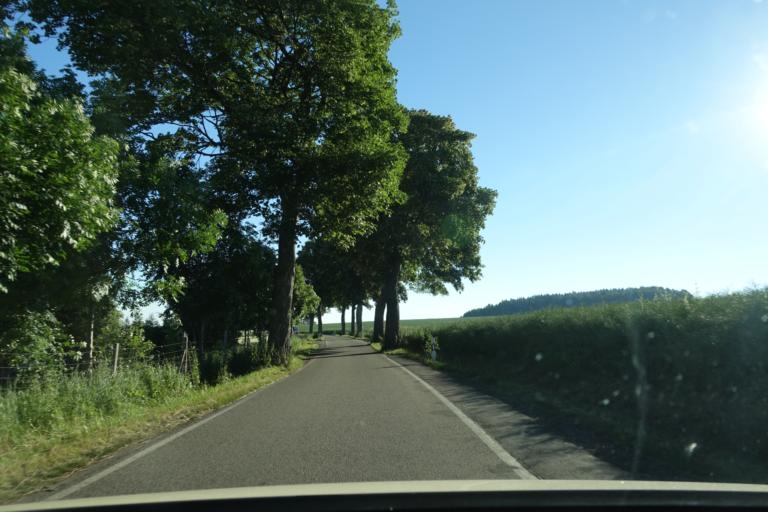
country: DE
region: Saxony
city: Eppendorf
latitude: 50.7739
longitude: 13.2570
